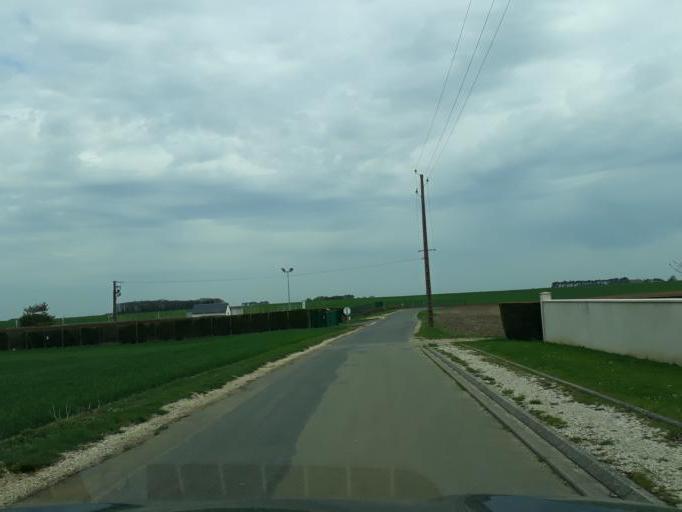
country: FR
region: Centre
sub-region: Departement du Loiret
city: Epieds-en-Beauce
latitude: 47.9497
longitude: 1.6256
